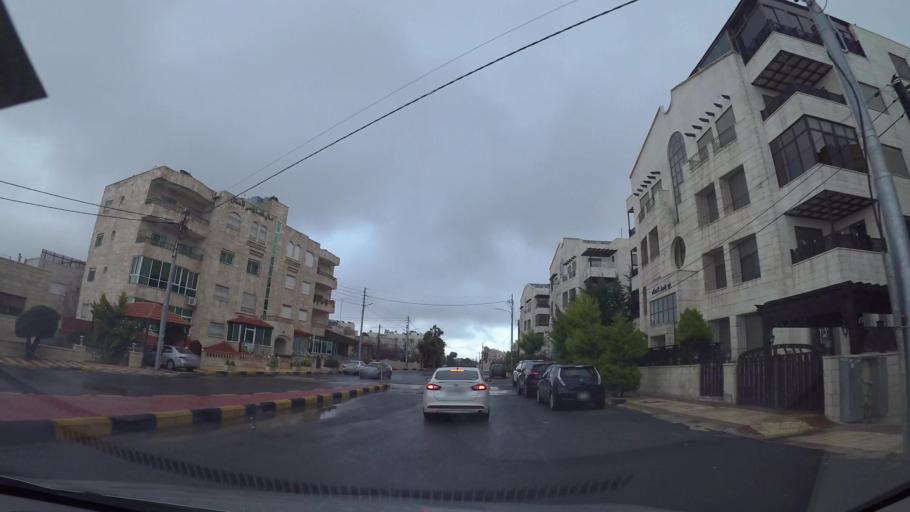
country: JO
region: Amman
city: Al Jubayhah
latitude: 32.0308
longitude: 35.8558
